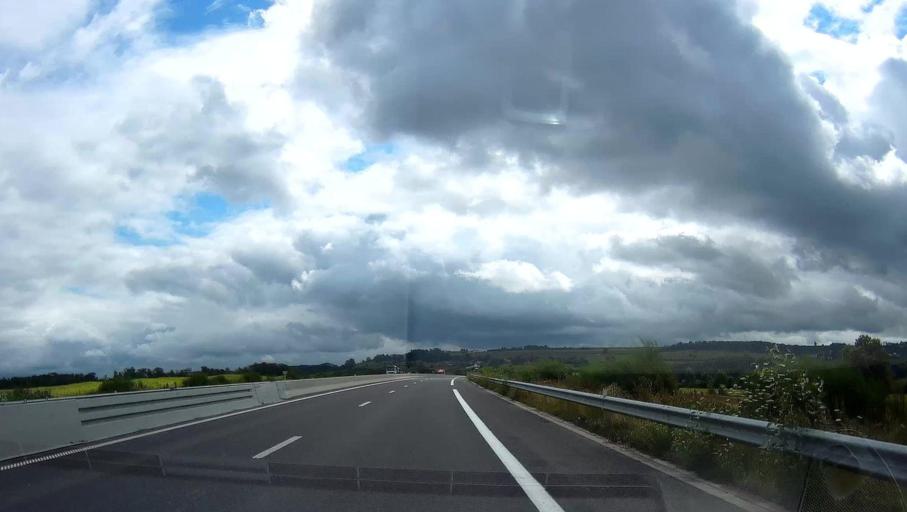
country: FR
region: Champagne-Ardenne
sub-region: Departement des Ardennes
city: Rimogne
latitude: 49.8022
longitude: 4.5313
